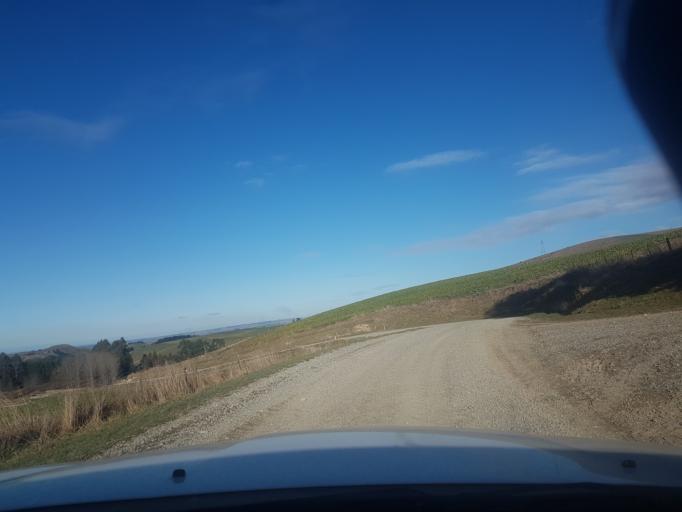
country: NZ
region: Canterbury
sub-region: Timaru District
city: Pleasant Point
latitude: -44.1670
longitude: 170.9160
